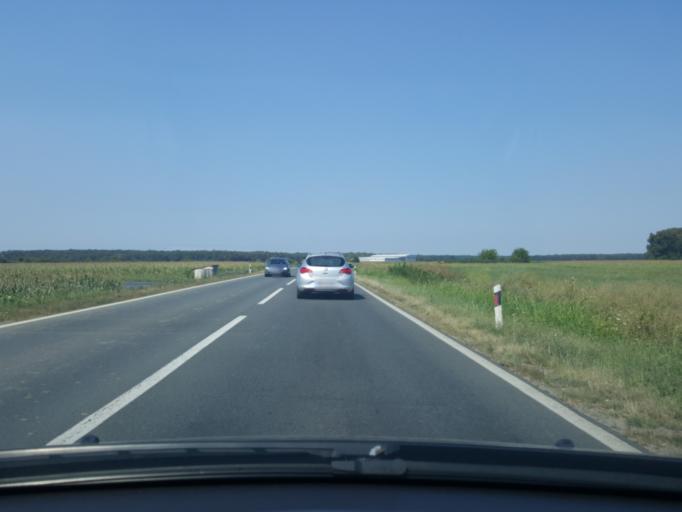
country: RS
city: Klenak
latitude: 44.7898
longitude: 19.7246
